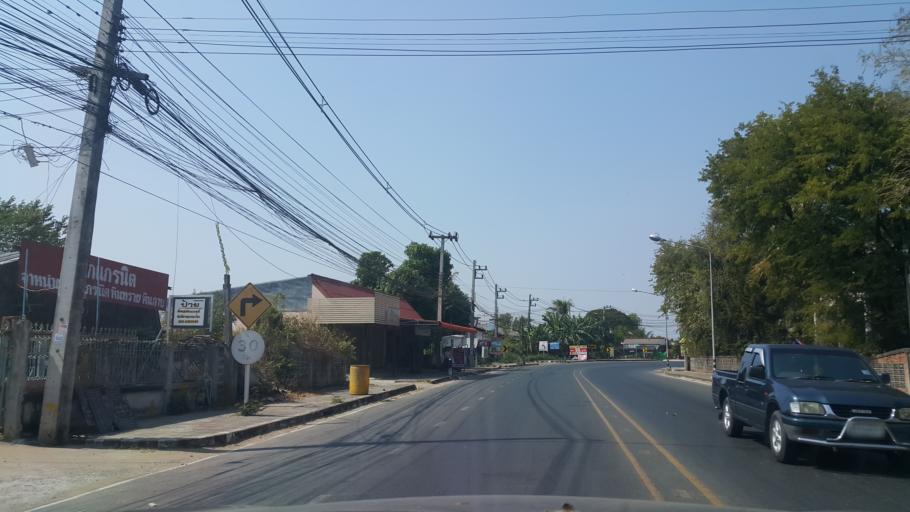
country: TH
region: Buriram
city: Satuek
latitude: 15.2934
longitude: 103.2839
